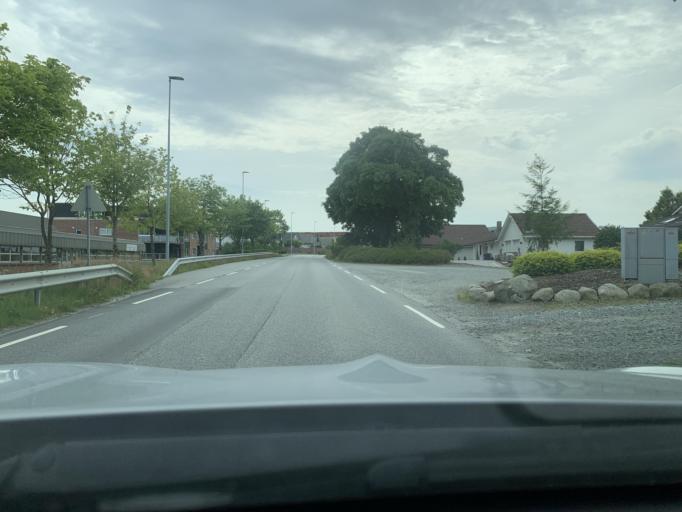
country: NO
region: Rogaland
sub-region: Sandnes
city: Sandnes
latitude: 58.7820
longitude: 5.7170
